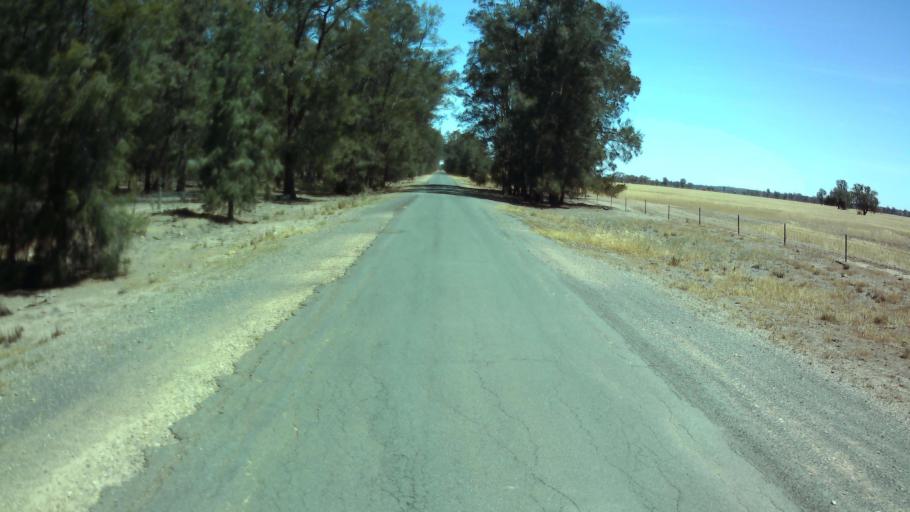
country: AU
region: New South Wales
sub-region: Weddin
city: Grenfell
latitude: -33.8802
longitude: 147.6902
